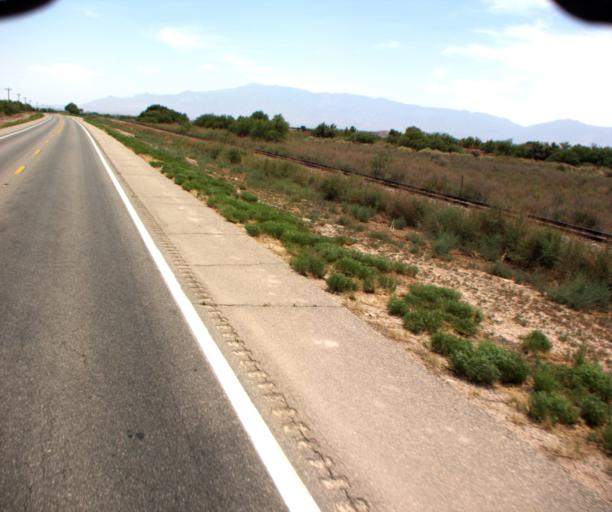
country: US
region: Arizona
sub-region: Graham County
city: Pima
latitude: 32.9941
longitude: -109.9394
